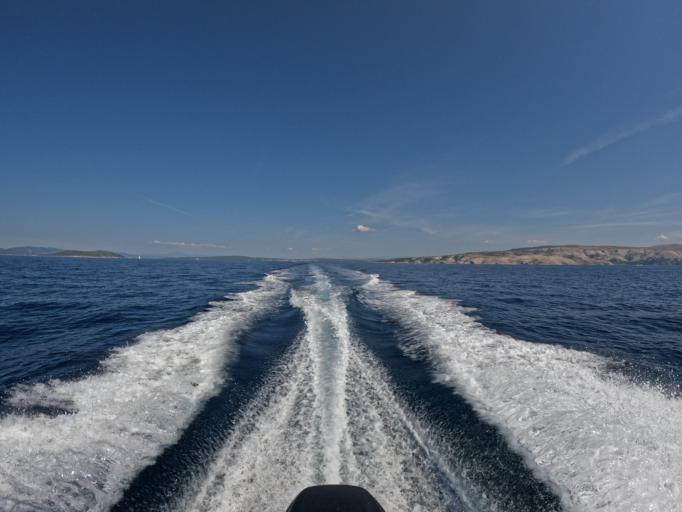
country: HR
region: Primorsko-Goranska
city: Punat
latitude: 44.9248
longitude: 14.6201
